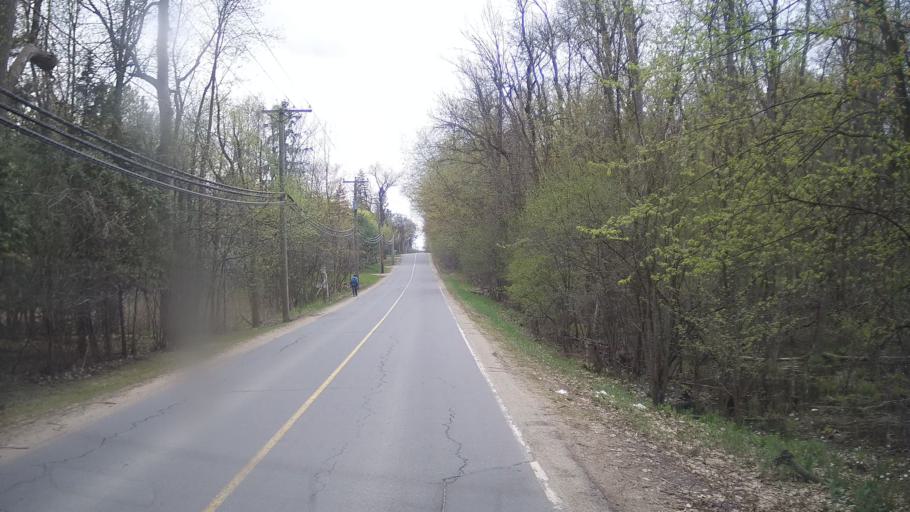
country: CA
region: Quebec
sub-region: Monteregie
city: Hudson
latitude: 45.4591
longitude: -74.1558
